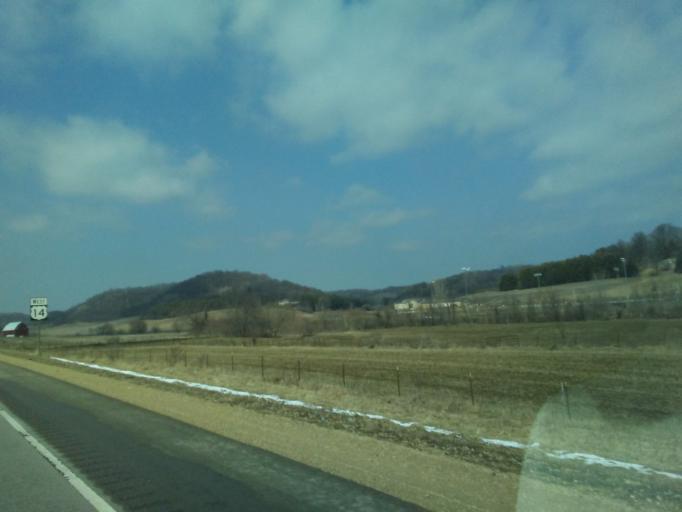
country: US
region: Wisconsin
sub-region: Richland County
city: Richland Center
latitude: 43.3456
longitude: -90.4084
